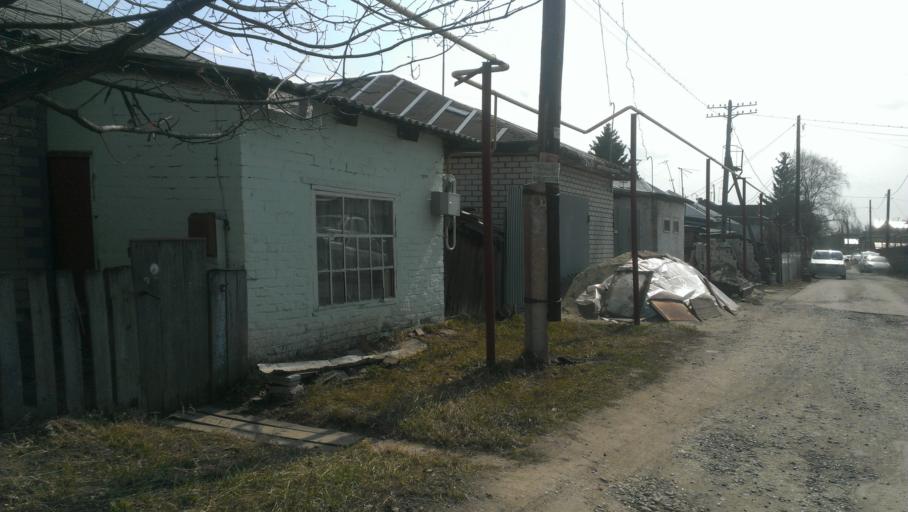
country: RU
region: Altai Krai
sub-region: Gorod Barnaulskiy
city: Barnaul
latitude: 53.3551
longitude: 83.6916
